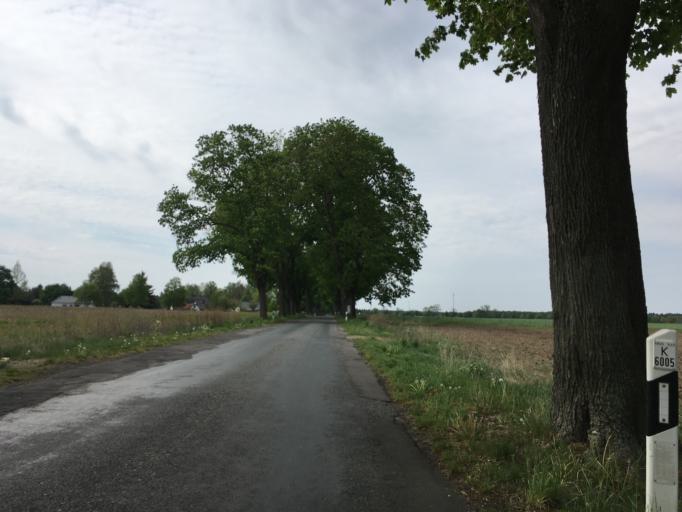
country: DE
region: Brandenburg
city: Rudnitz
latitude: 52.7282
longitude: 13.6423
